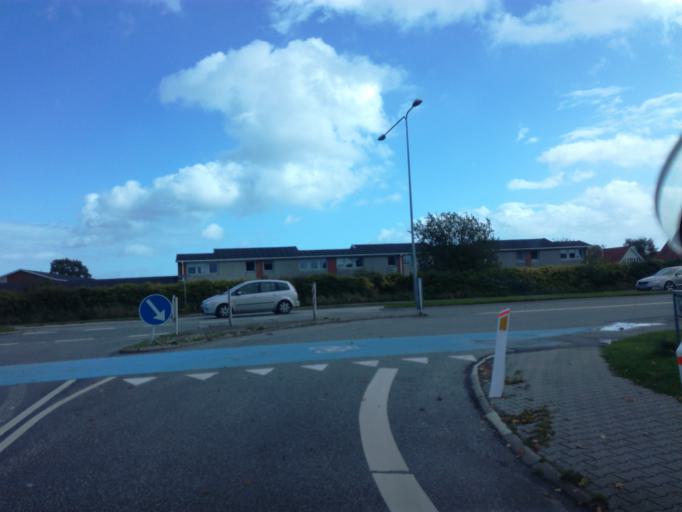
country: DK
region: South Denmark
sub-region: Fredericia Kommune
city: Fredericia
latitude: 55.5672
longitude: 9.7242
